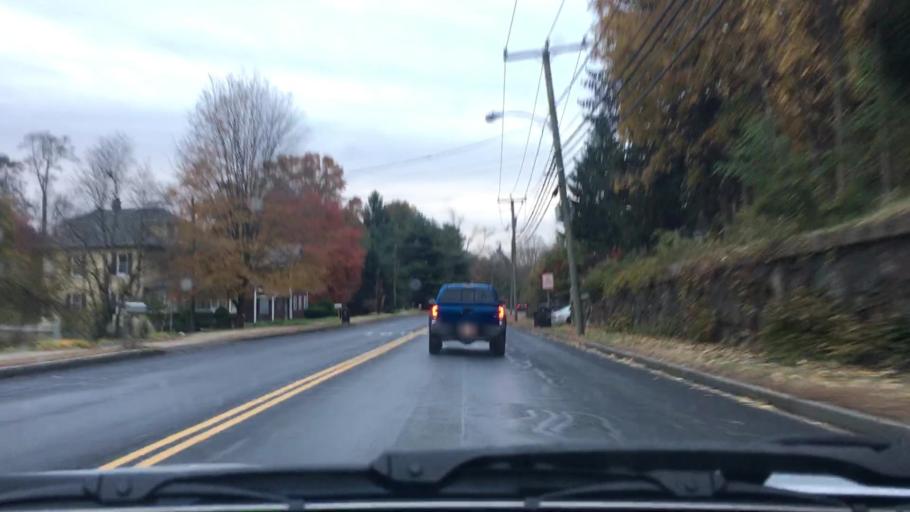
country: US
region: Massachusetts
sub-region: Hampden County
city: Agawam
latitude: 42.0642
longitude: -72.6771
